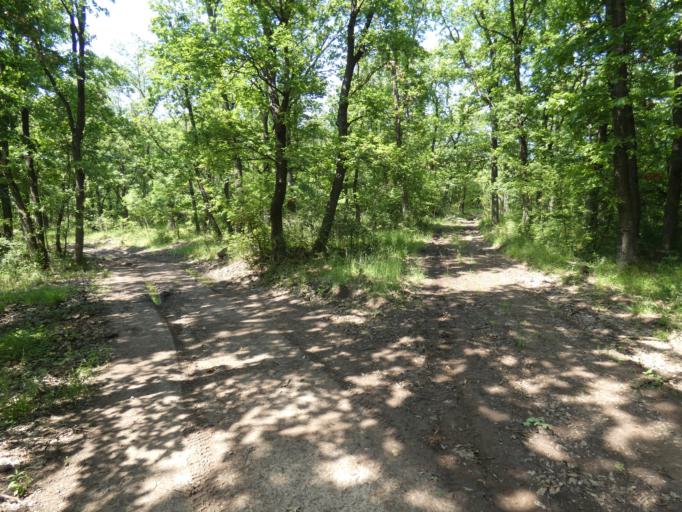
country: HU
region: Pest
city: Szob
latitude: 47.8679
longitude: 18.8309
